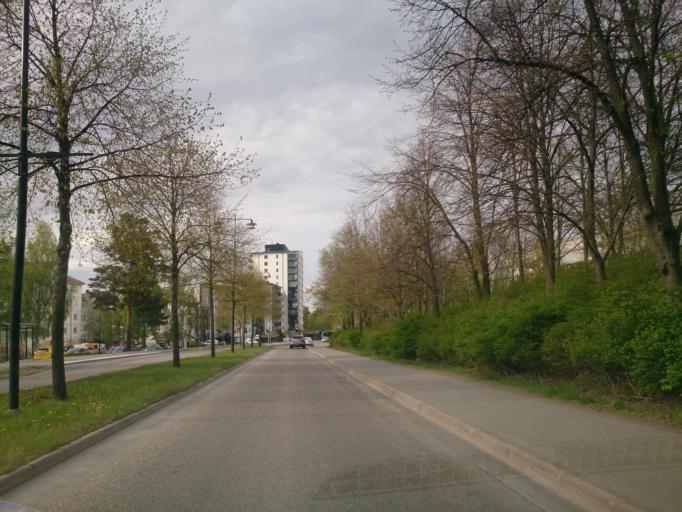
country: SE
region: Stockholm
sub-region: Haninge Kommun
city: Handen
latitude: 59.1733
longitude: 18.1400
